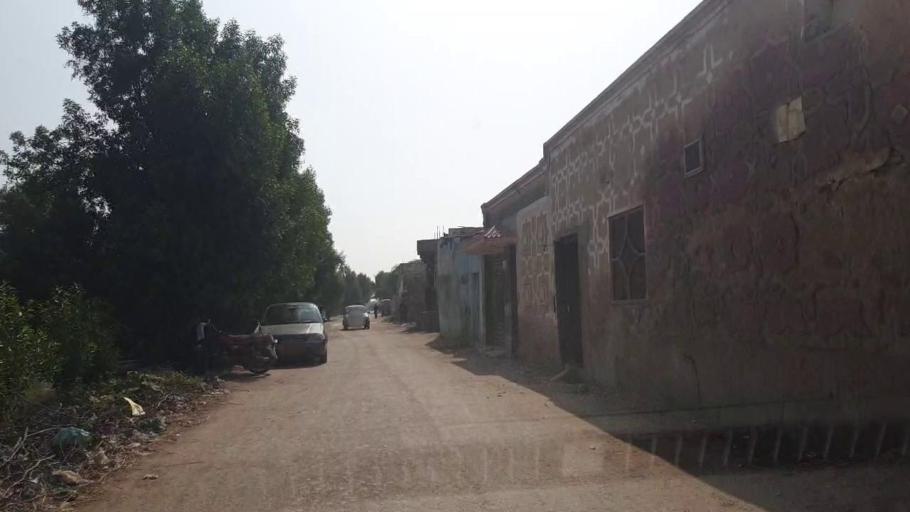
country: PK
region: Sindh
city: Badin
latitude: 24.6563
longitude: 68.8411
